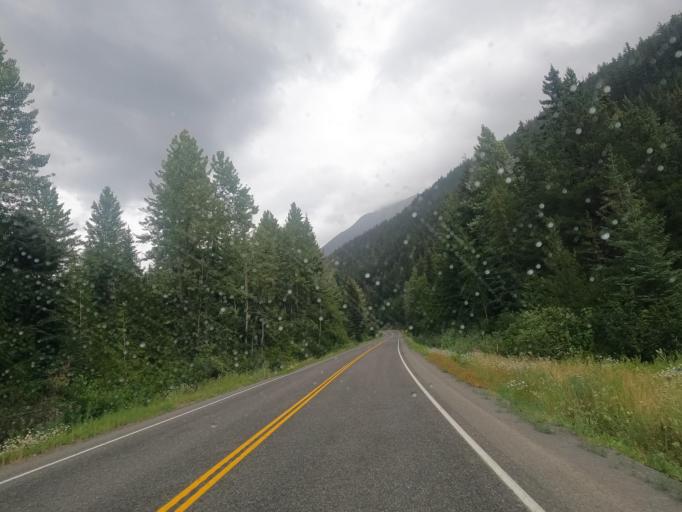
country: CA
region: British Columbia
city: Lillooet
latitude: 50.4775
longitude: -122.2212
